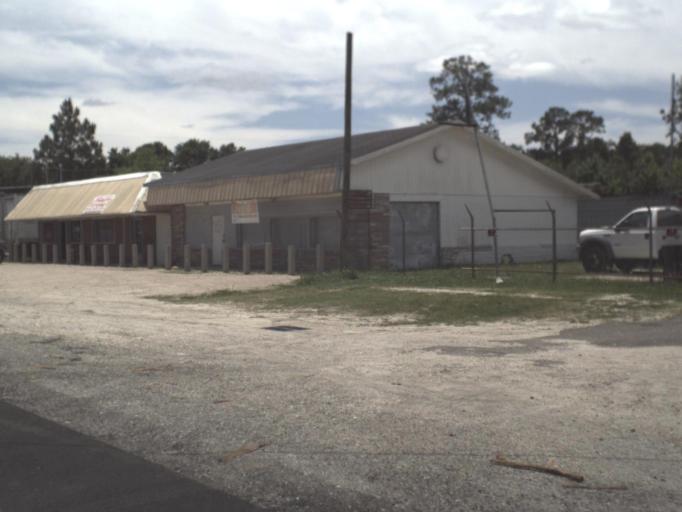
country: US
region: Florida
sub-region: Nassau County
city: Nassau Village-Ratliff
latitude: 30.4277
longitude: -81.7571
